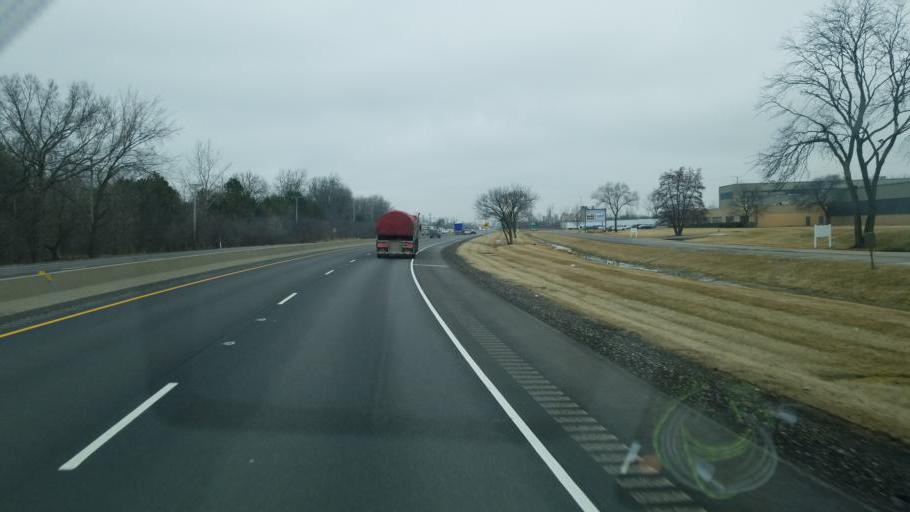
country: US
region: Illinois
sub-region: Lake County
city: Knollwood
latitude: 42.2911
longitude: -87.8756
